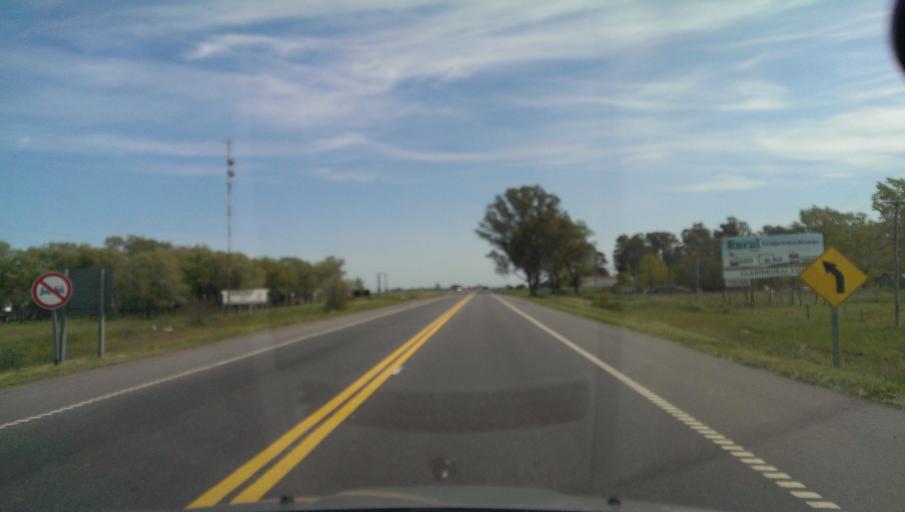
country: AR
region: Buenos Aires
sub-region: Partido de Azul
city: Azul
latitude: -36.3918
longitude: -59.4976
